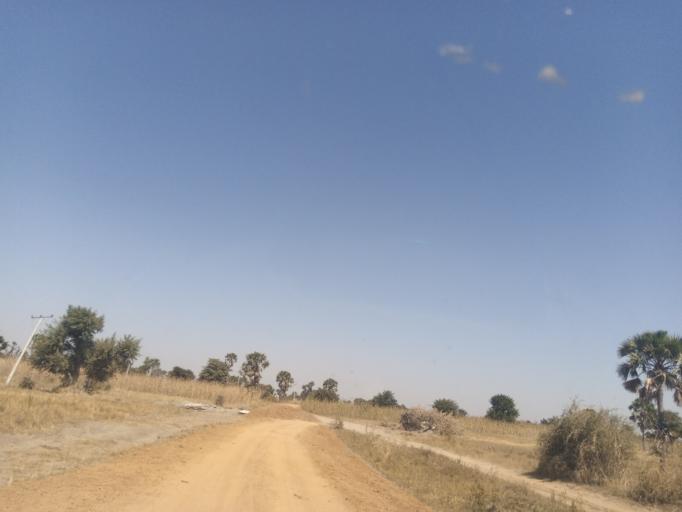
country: NG
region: Adamawa
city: Yola
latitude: 9.2957
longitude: 12.8866
